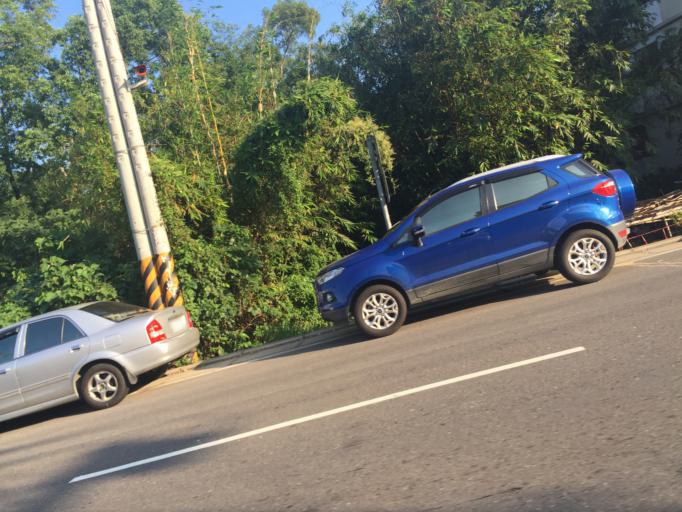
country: TW
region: Taiwan
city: Daxi
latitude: 24.9263
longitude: 121.2588
